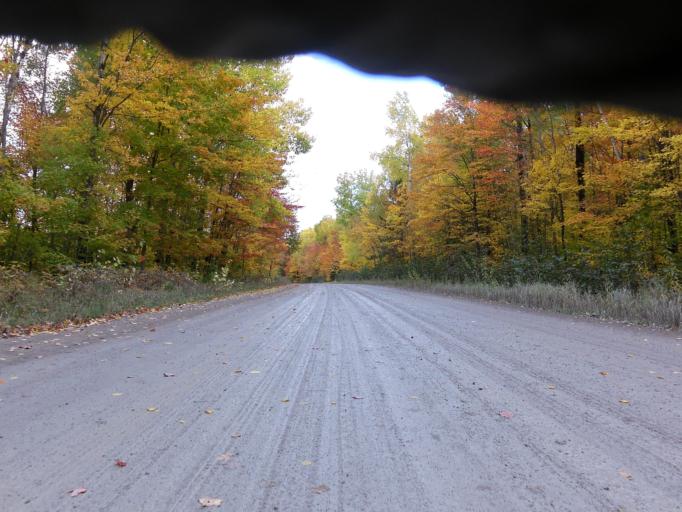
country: CA
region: Ontario
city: Petawawa
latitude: 45.8096
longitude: -77.3594
